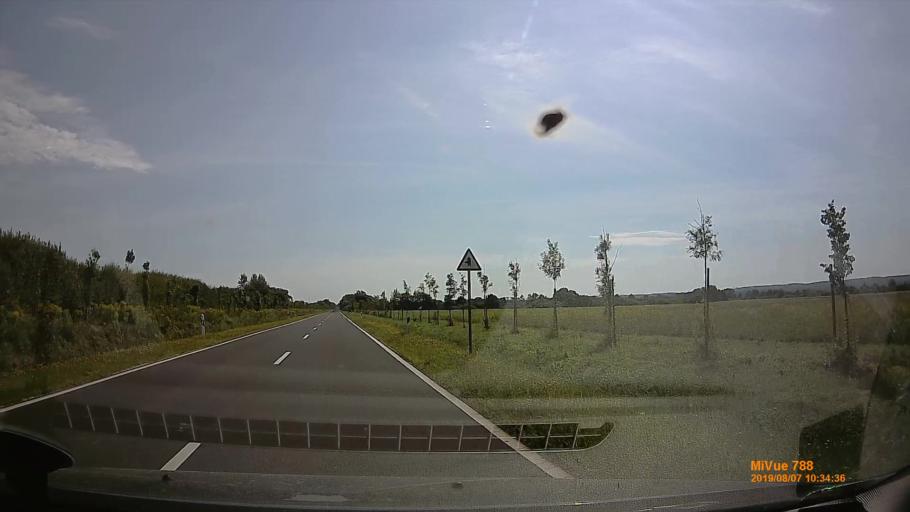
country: SI
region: Lendava-Lendva
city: Lendava
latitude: 46.6171
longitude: 16.4295
